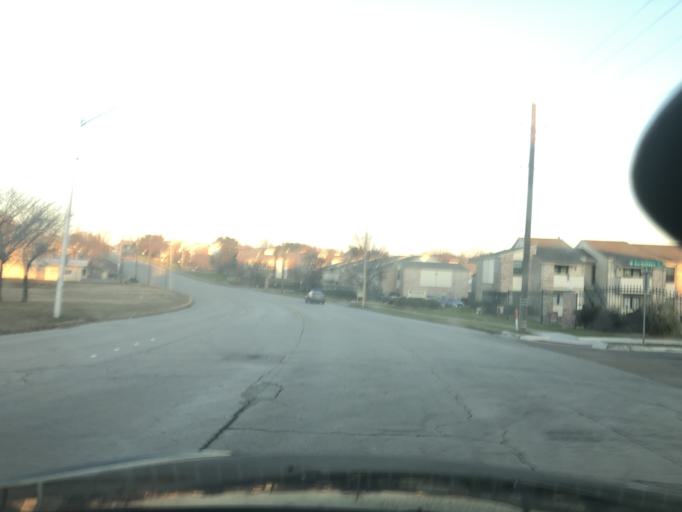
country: US
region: Texas
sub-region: Tarrant County
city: White Settlement
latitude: 32.7333
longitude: -97.4792
